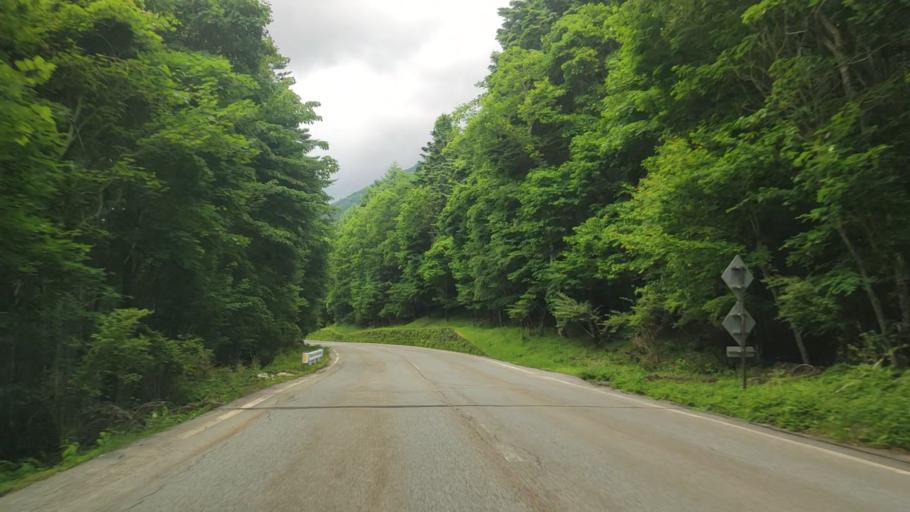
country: JP
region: Yamanashi
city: Fujikawaguchiko
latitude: 35.4156
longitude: 138.7319
